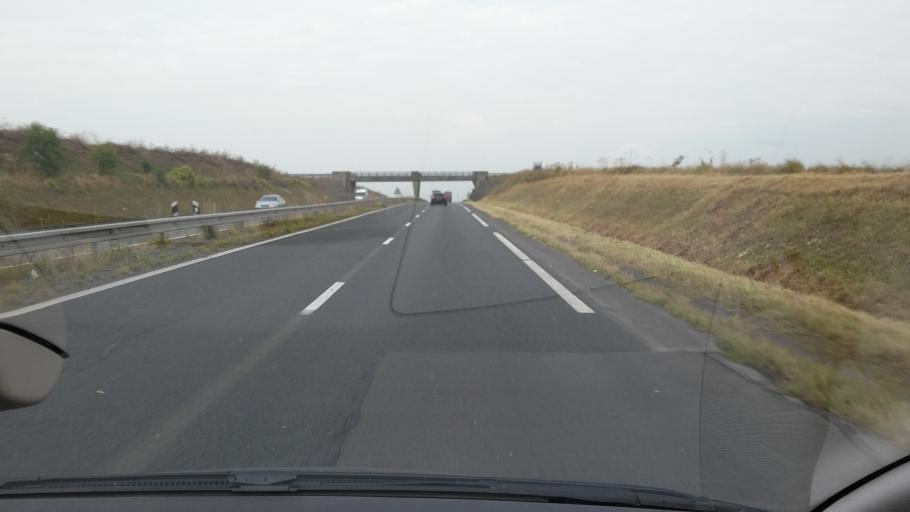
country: FR
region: Champagne-Ardenne
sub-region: Departement de la Marne
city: Warmeriville
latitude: 49.3655
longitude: 4.2107
